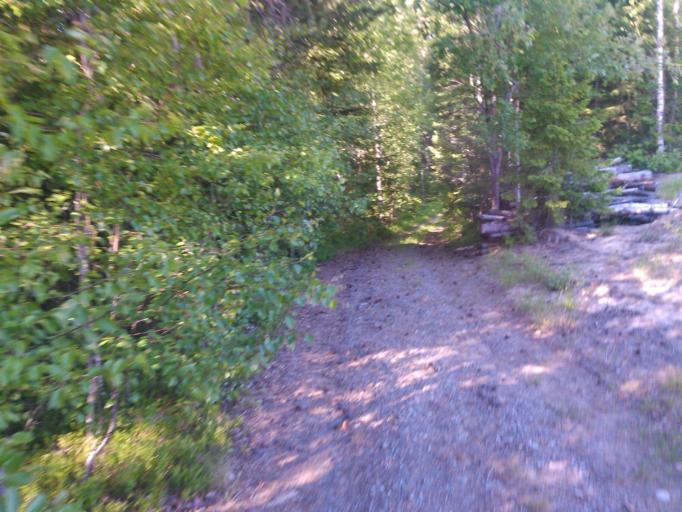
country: SE
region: Vaesterbotten
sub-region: Umea Kommun
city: Roback
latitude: 63.8267
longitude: 20.1446
